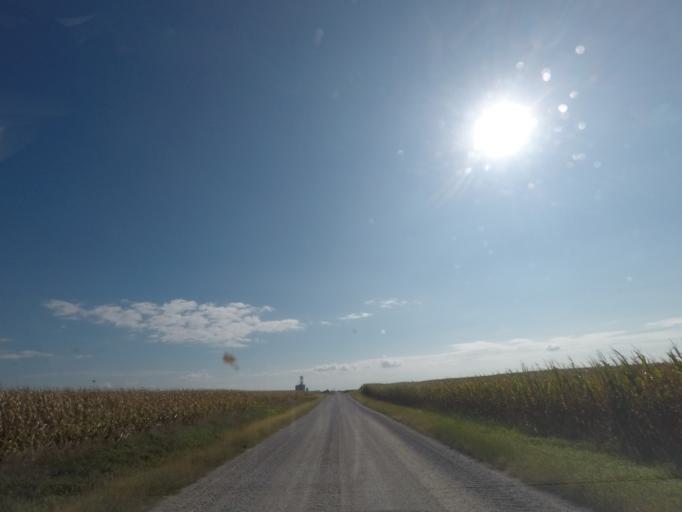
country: US
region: Iowa
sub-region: Story County
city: Nevada
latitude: 42.0490
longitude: -93.4217
